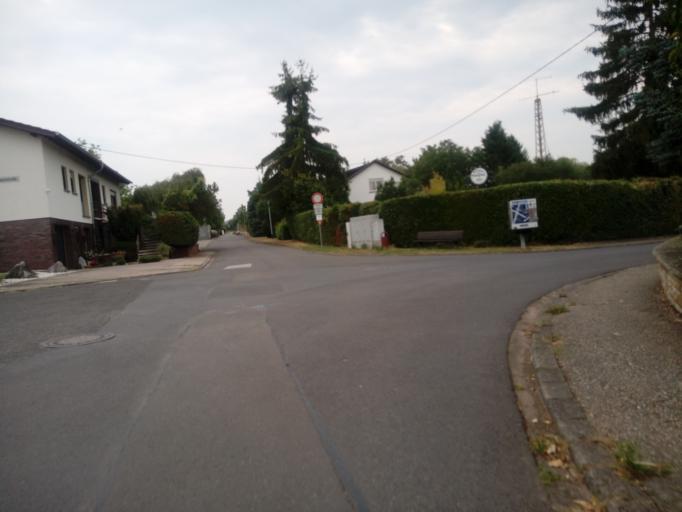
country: DE
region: Rheinland-Pfalz
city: Gutenberg
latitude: 49.8803
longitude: 7.7951
